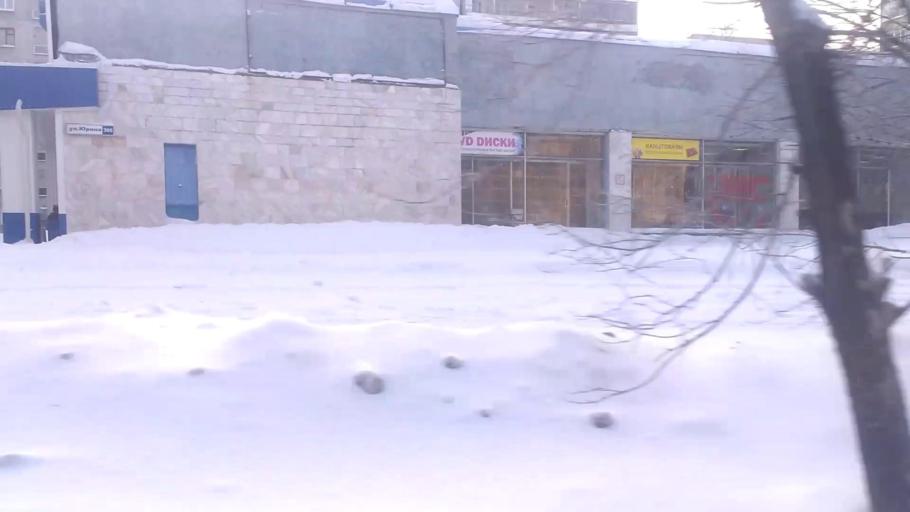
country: RU
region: Altai Krai
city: Novosilikatnyy
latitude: 53.3742
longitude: 83.6664
